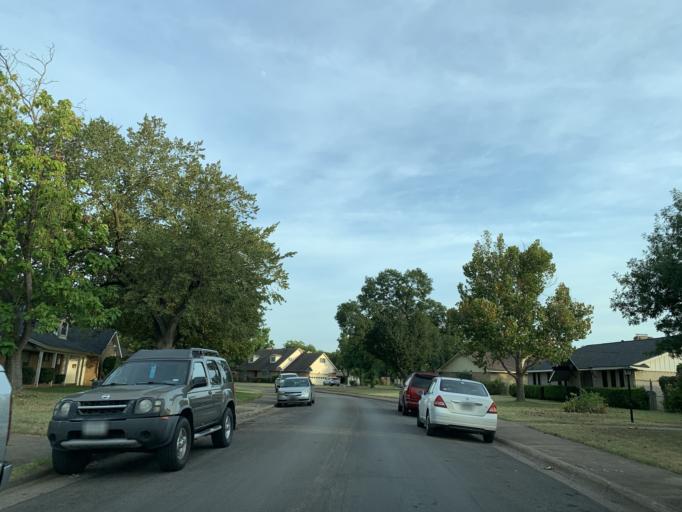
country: US
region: Texas
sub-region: Dallas County
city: Cockrell Hill
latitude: 32.6950
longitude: -96.8851
